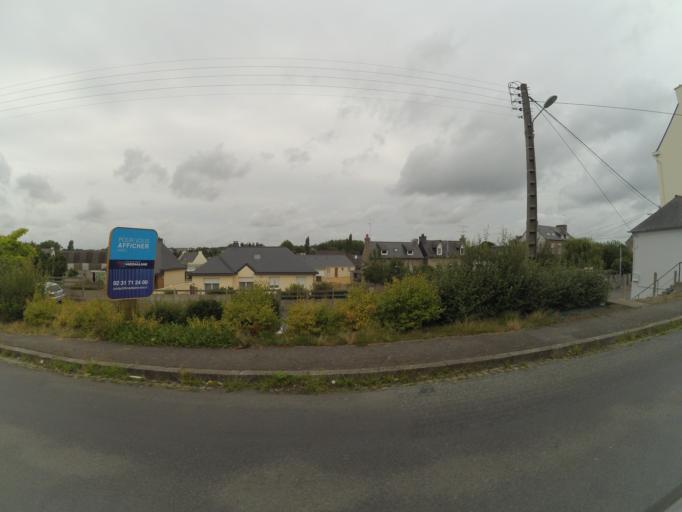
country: FR
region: Brittany
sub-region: Departement des Cotes-d'Armor
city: Ploumagoar
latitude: 48.5574
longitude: -3.1360
